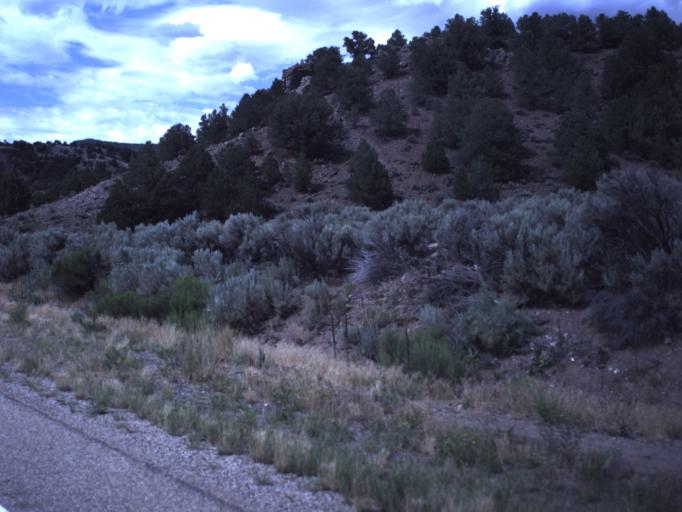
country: US
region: Utah
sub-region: Garfield County
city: Panguitch
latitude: 37.9791
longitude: -112.4849
